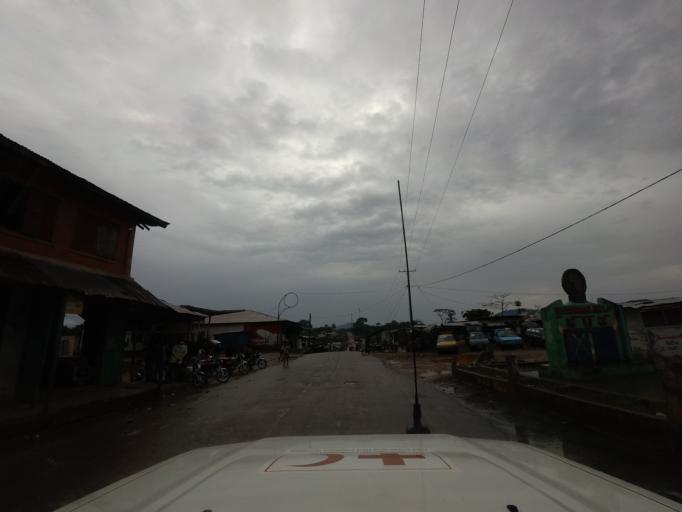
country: LR
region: Nimba
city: Sanniquellie
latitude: 7.3620
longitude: -8.7121
